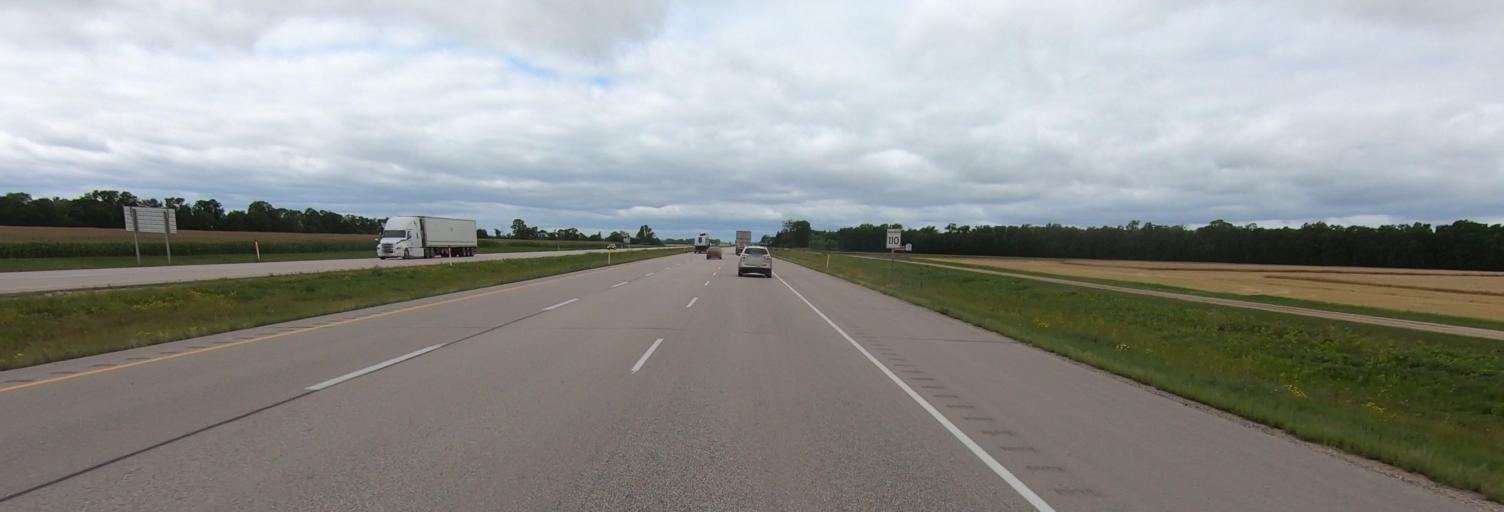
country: CA
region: Manitoba
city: Portage la Prairie
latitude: 49.9545
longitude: -98.0141
